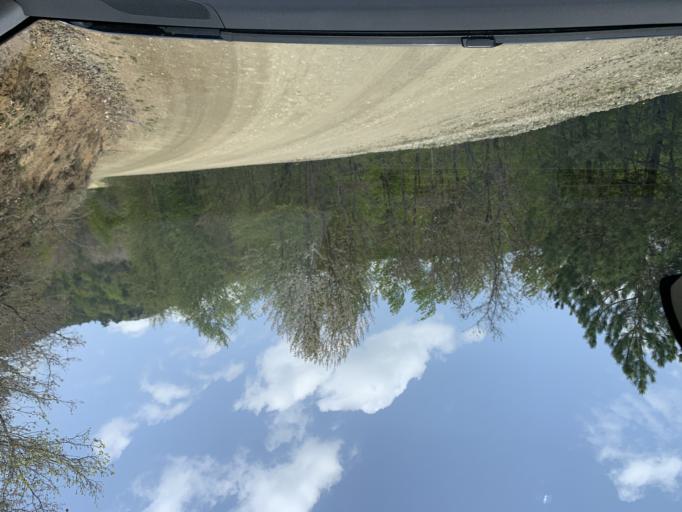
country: TR
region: Bolu
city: Bolu
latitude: 40.8329
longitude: 31.6718
